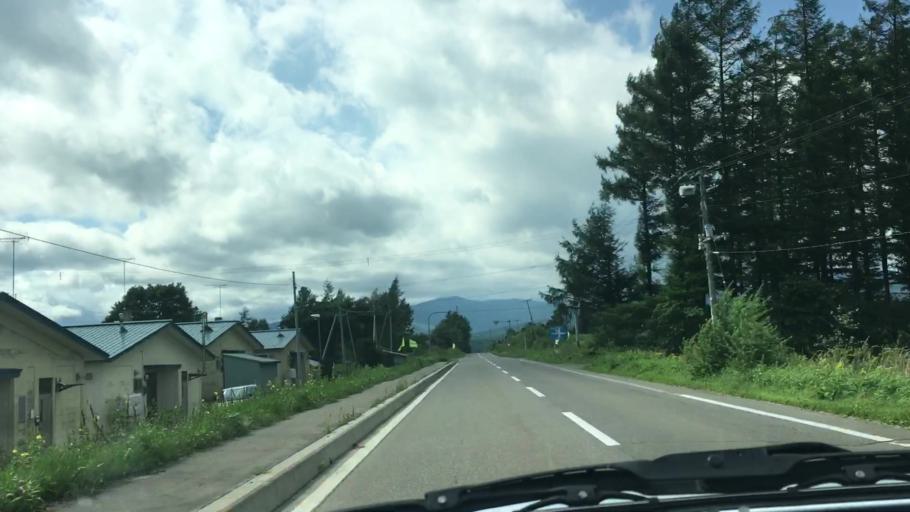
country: JP
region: Hokkaido
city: Otofuke
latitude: 43.2817
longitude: 143.3280
